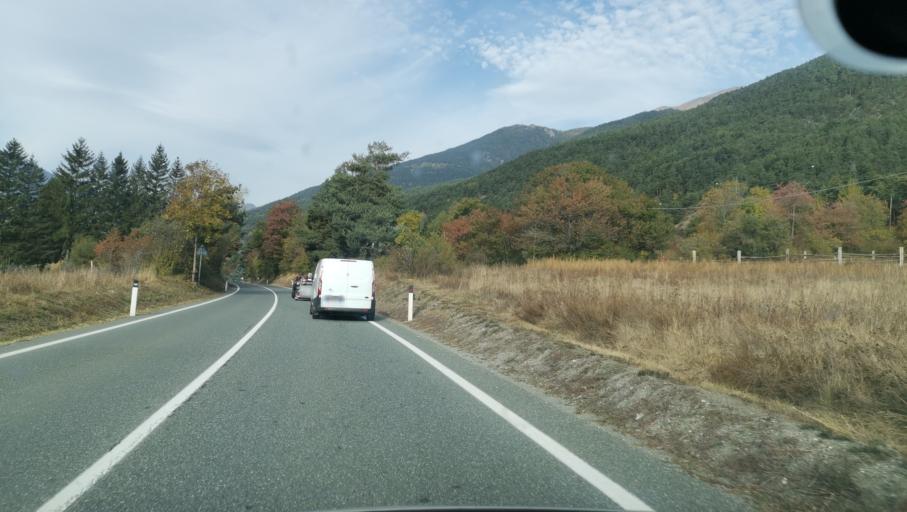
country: IT
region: Piedmont
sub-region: Provincia di Torino
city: Oulx
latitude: 45.0445
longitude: 6.8036
